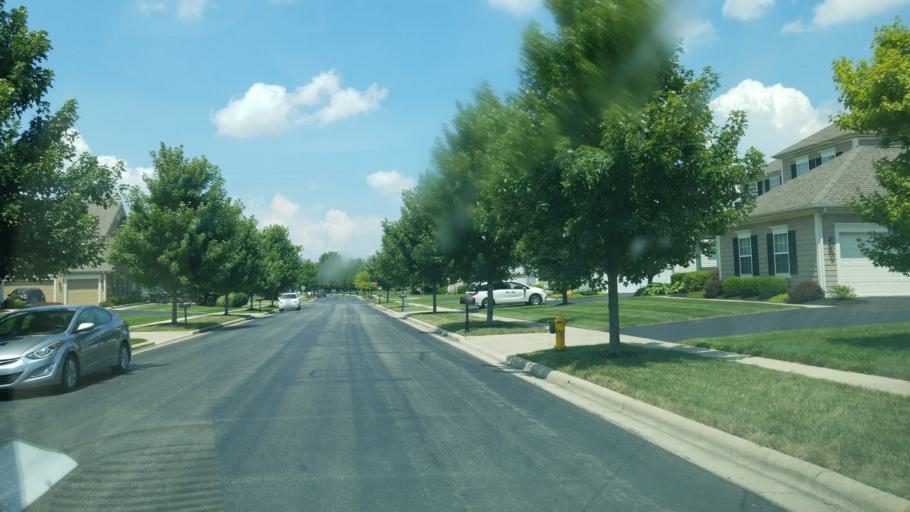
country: US
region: Ohio
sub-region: Delaware County
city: Lewis Center
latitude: 40.2220
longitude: -83.0060
